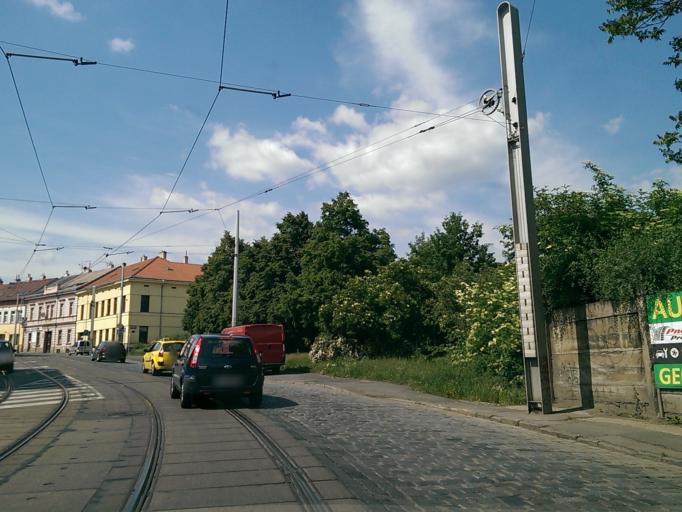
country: CZ
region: Praha
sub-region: Praha 8
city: Liben
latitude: 50.1134
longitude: 14.4763
